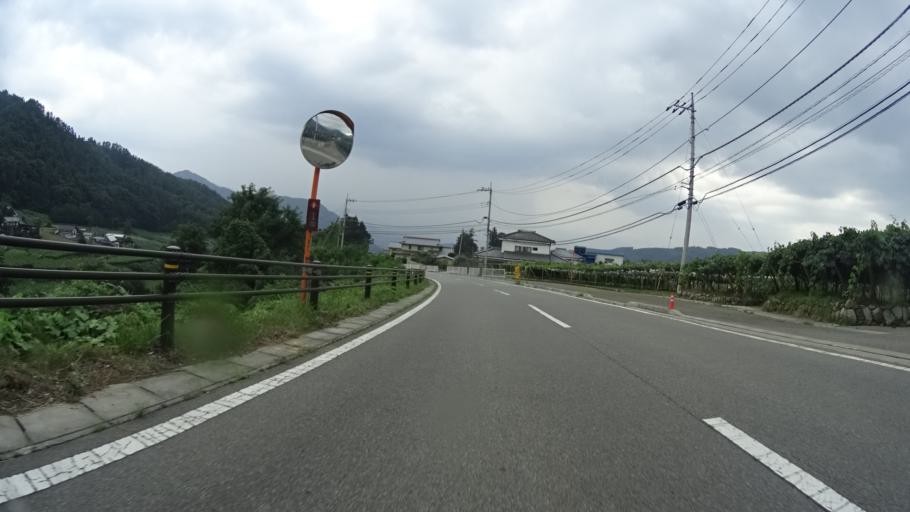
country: JP
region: Yamanashi
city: Enzan
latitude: 35.7596
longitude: 138.7063
